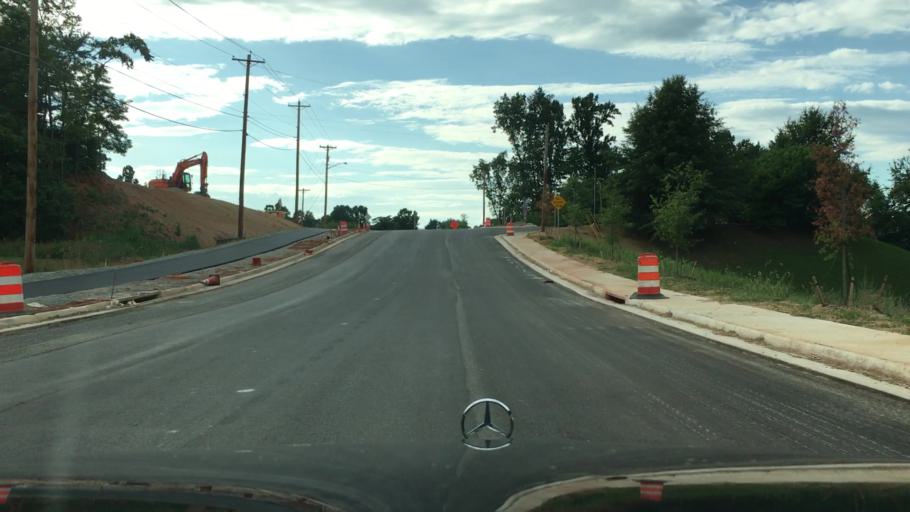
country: US
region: Virginia
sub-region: City of Lynchburg
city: West Lynchburg
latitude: 37.3778
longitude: -79.1533
